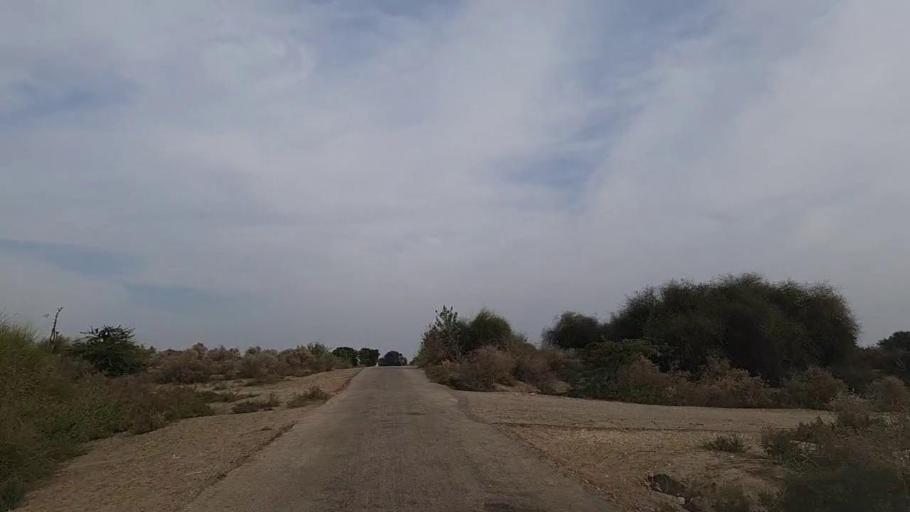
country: PK
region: Sindh
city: Jam Sahib
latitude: 26.4414
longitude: 68.5998
